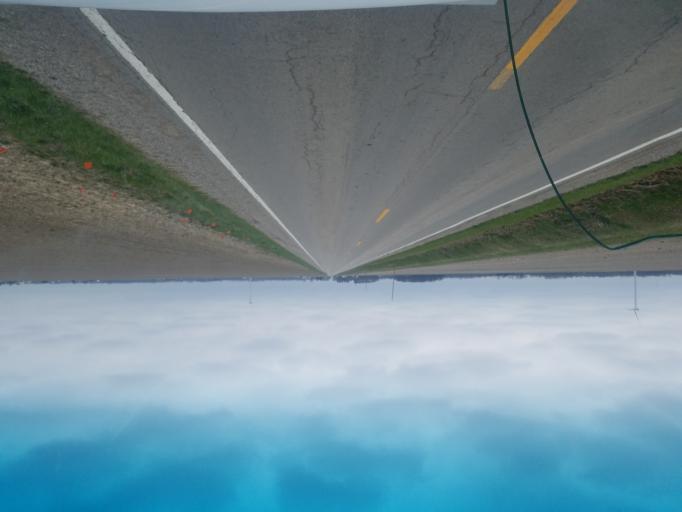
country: US
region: Ohio
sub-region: Paulding County
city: Payne
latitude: 41.0412
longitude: -84.7267
